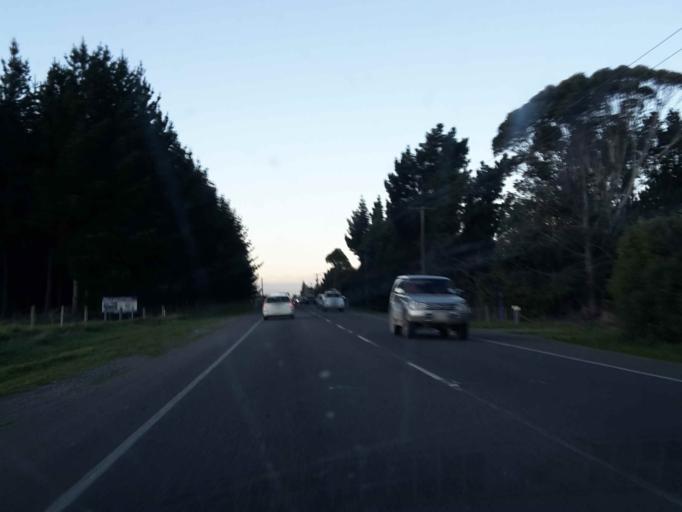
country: NZ
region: Canterbury
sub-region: Selwyn District
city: Prebbleton
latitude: -43.5635
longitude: 172.4530
